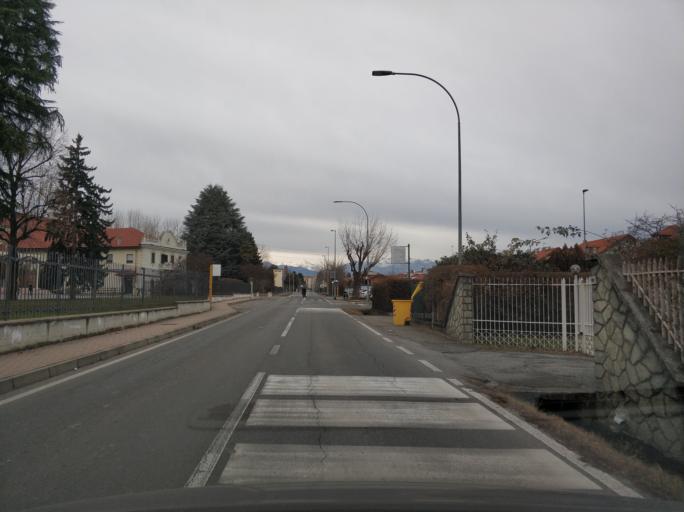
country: IT
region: Piedmont
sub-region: Provincia di Torino
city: San Maurizio
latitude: 45.2080
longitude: 7.6356
